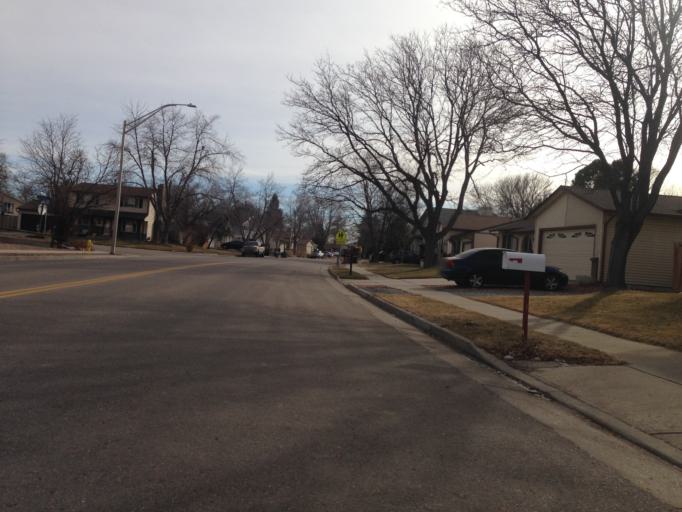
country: US
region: Colorado
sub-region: Adams County
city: Westminster
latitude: 39.8530
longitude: -105.0648
